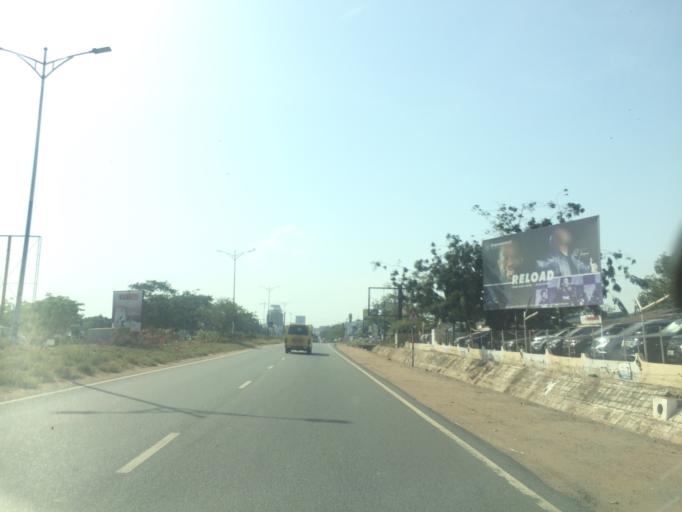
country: GH
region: Greater Accra
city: Accra
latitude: 5.5618
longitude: -0.1715
